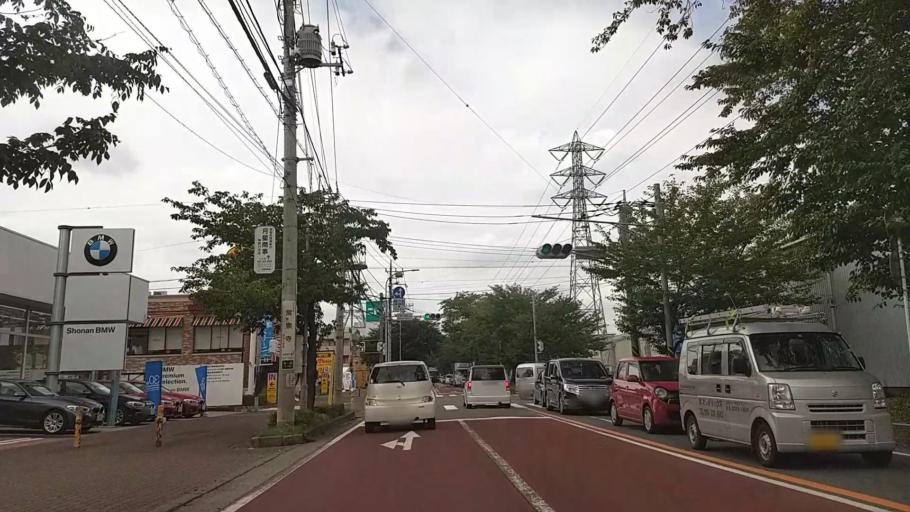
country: JP
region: Kanagawa
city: Minami-rinkan
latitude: 35.4370
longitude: 139.4669
